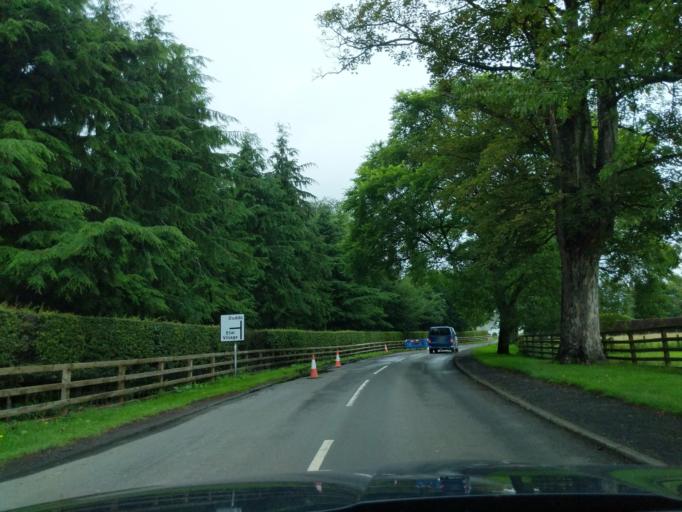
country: GB
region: England
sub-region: Northumberland
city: Ford
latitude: 55.6468
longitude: -2.1152
